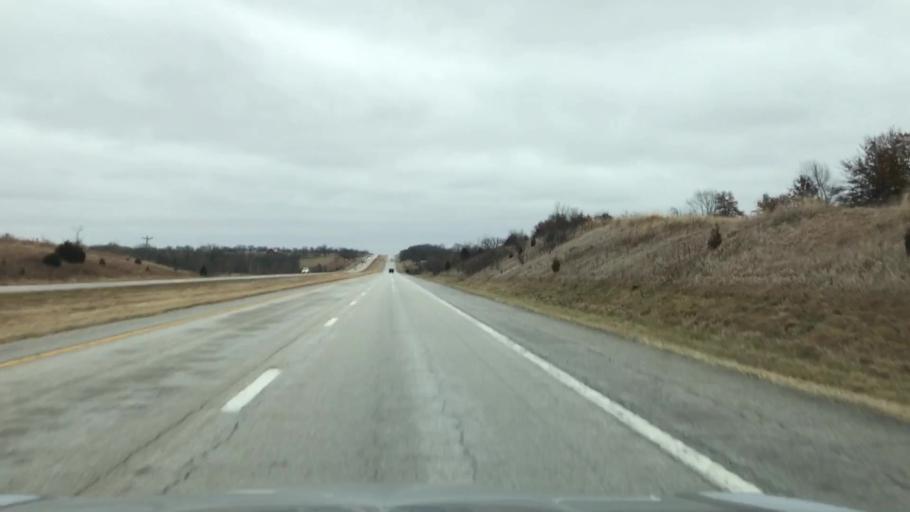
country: US
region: Missouri
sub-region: Clinton County
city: Cameron
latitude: 39.7505
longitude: -94.1256
